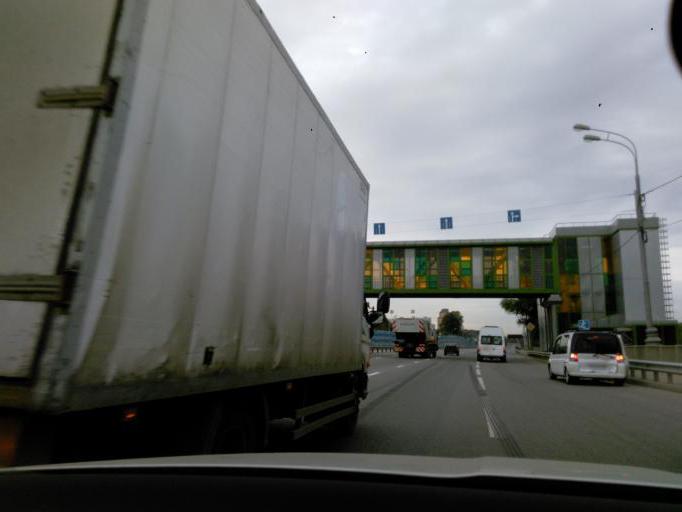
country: RU
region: Moscow
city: Severnyy
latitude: 55.9433
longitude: 37.5431
